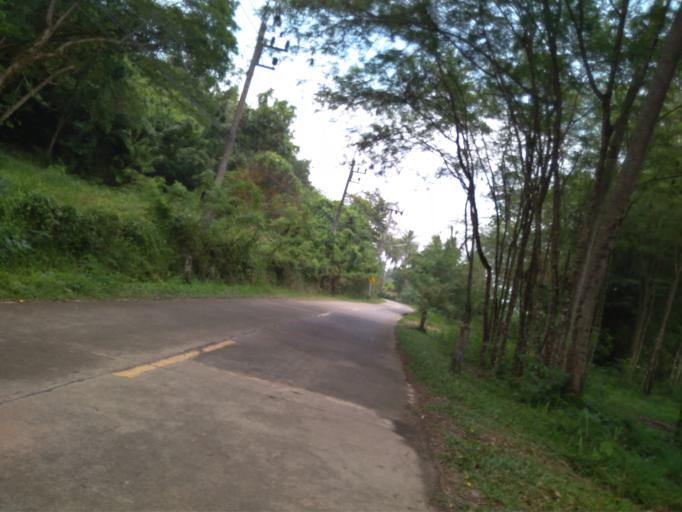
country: TH
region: Phangnga
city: Ko Yao
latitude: 8.1127
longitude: 98.6234
